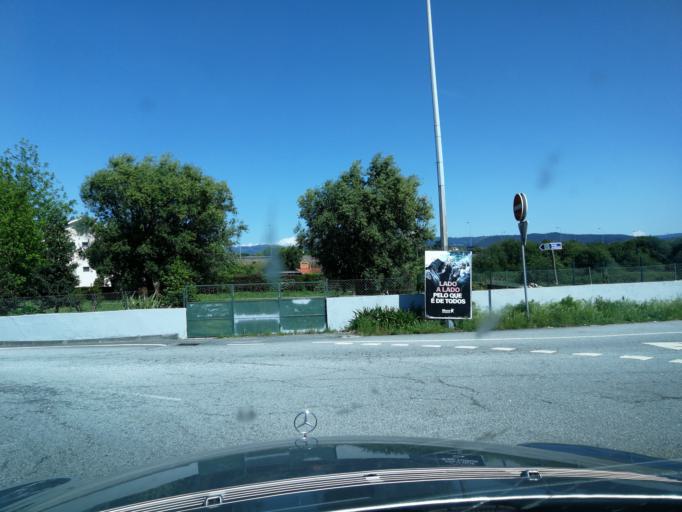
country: PT
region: Viana do Castelo
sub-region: Viana do Castelo
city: Meadela
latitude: 41.7067
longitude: -8.8014
